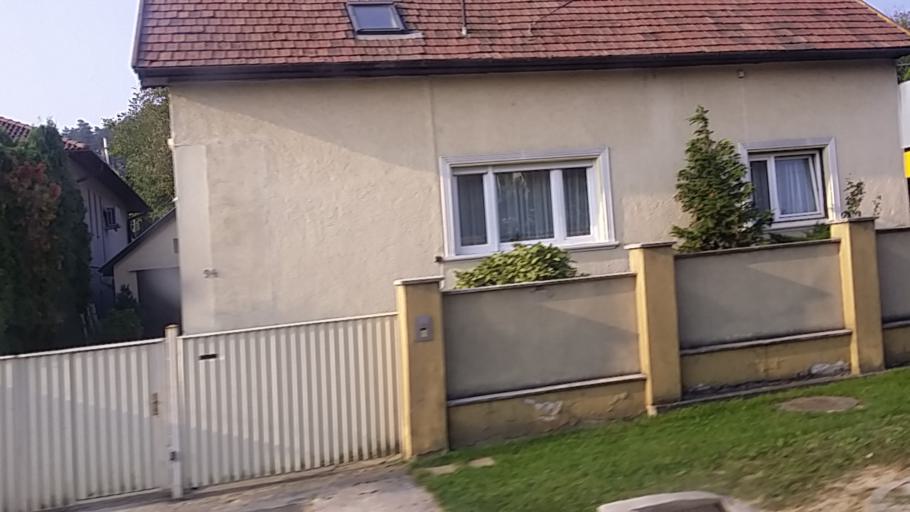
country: HU
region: Pest
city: Pilisszentivan
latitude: 47.6266
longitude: 18.8963
